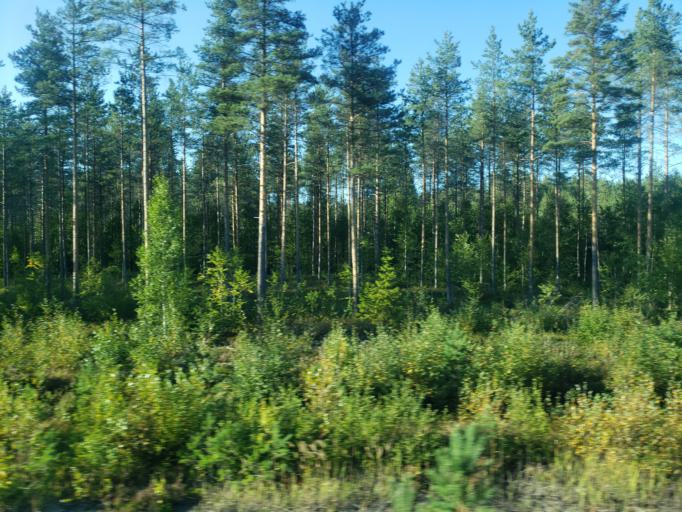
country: FI
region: South Karelia
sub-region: Lappeenranta
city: Ylaemaa
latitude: 60.9324
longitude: 27.9196
